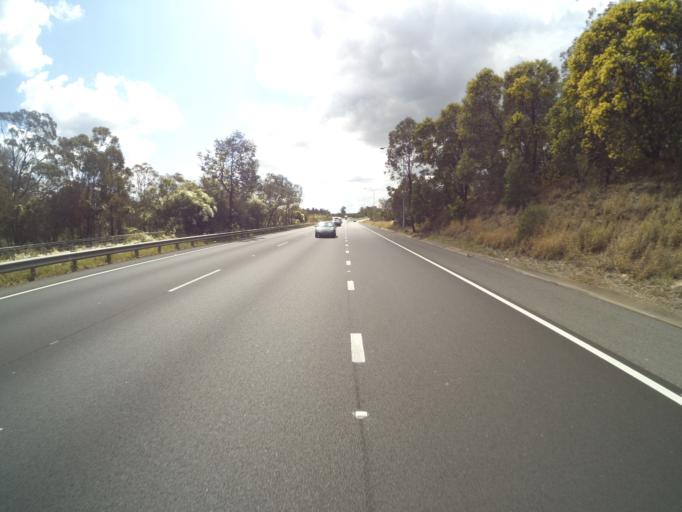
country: AU
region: New South Wales
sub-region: Wollondilly
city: Douglas Park
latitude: -34.2342
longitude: 150.6644
